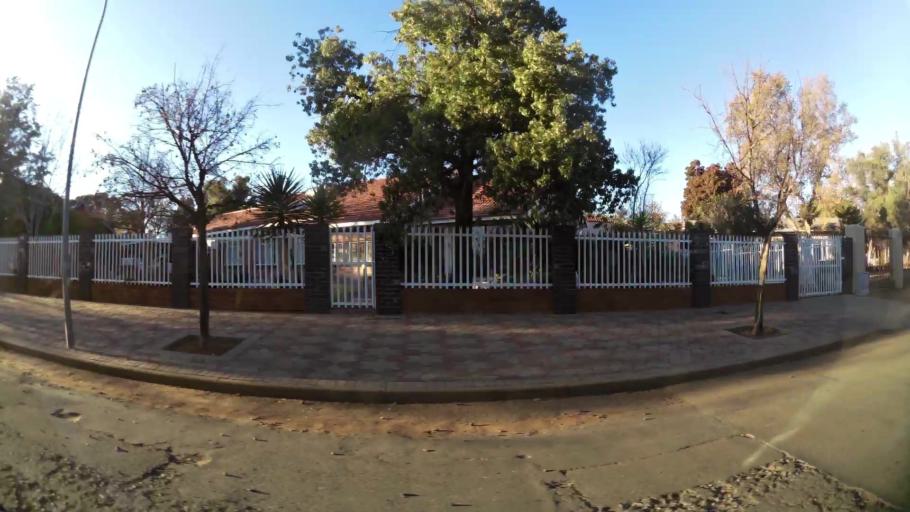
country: ZA
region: Northern Cape
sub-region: Frances Baard District Municipality
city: Kimberley
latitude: -28.7514
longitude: 24.7430
